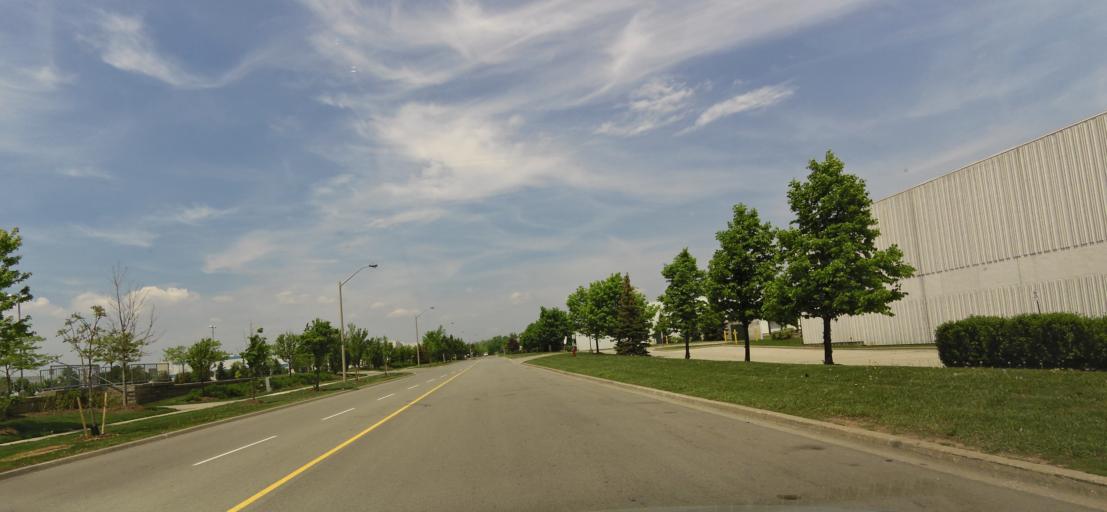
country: CA
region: Ontario
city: Oakville
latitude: 43.5048
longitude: -79.6713
